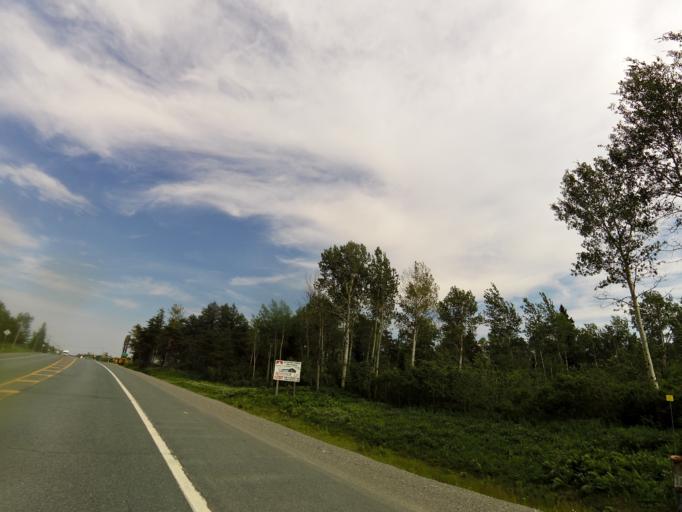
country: CA
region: Quebec
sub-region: Abitibi-Temiscamingue
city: Malartic
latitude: 48.2263
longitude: -78.3933
